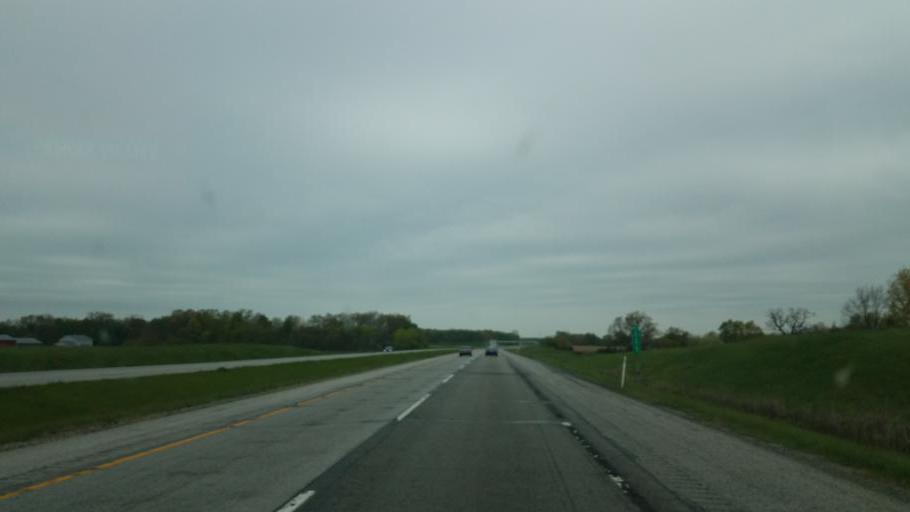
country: US
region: Michigan
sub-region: Saint Joseph County
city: White Pigeon
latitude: 41.7519
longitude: -85.6098
